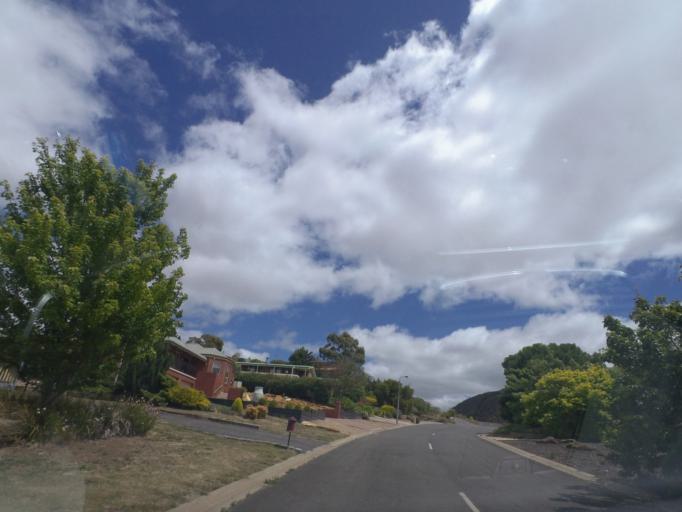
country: AU
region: Victoria
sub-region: Moorabool
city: Bacchus Marsh
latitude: -37.6352
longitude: 144.4195
